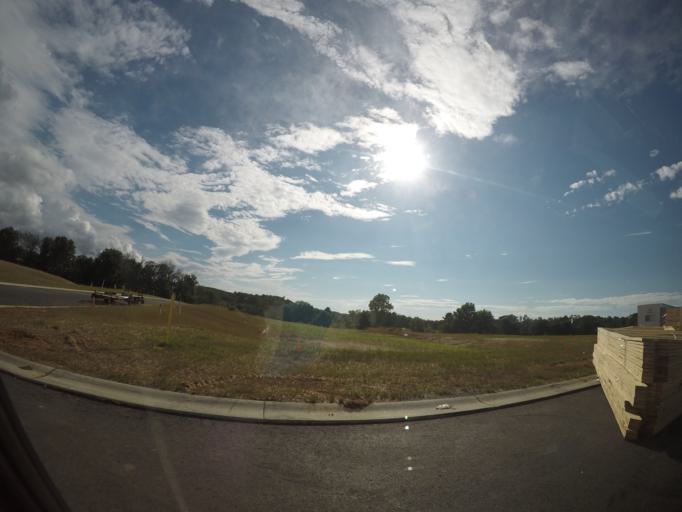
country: US
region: Maryland
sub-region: Howard County
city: Highland
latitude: 39.1974
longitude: -76.9407
